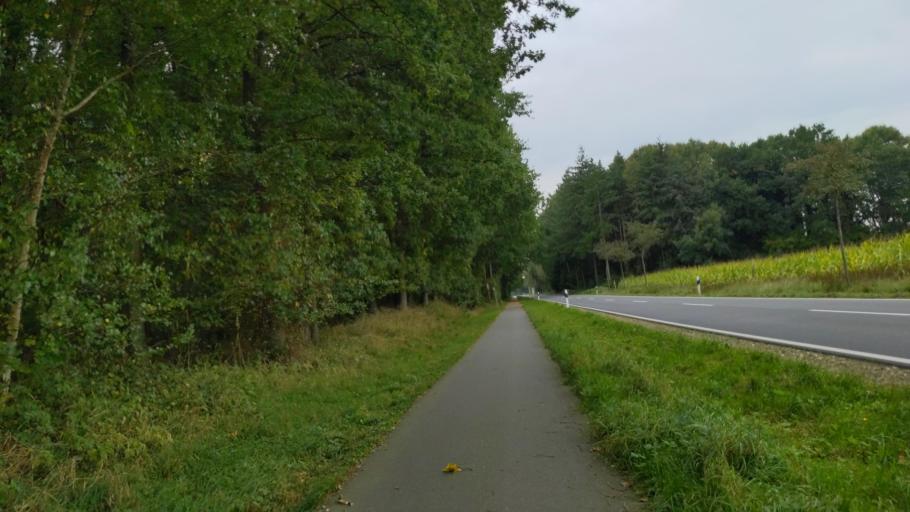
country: DE
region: Schleswig-Holstein
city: Krummesse
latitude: 53.7841
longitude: 10.6648
